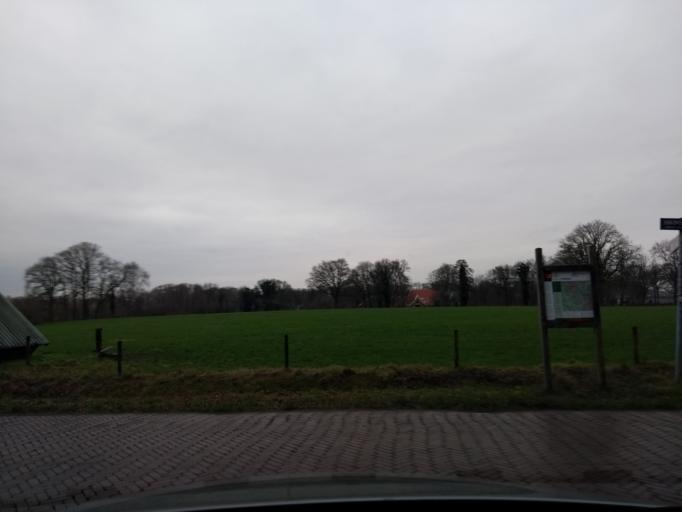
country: NL
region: Overijssel
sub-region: Gemeente Hengelo
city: Hengelo
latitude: 52.2301
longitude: 6.8105
